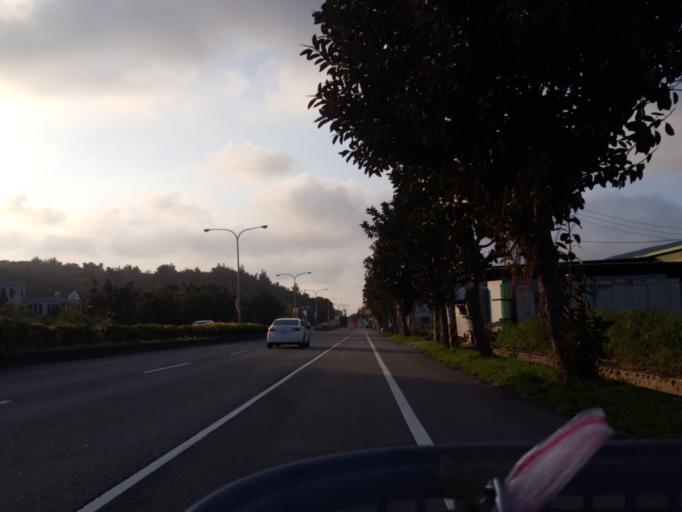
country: TW
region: Taiwan
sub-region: Hsinchu
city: Zhubei
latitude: 24.8827
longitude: 121.0297
